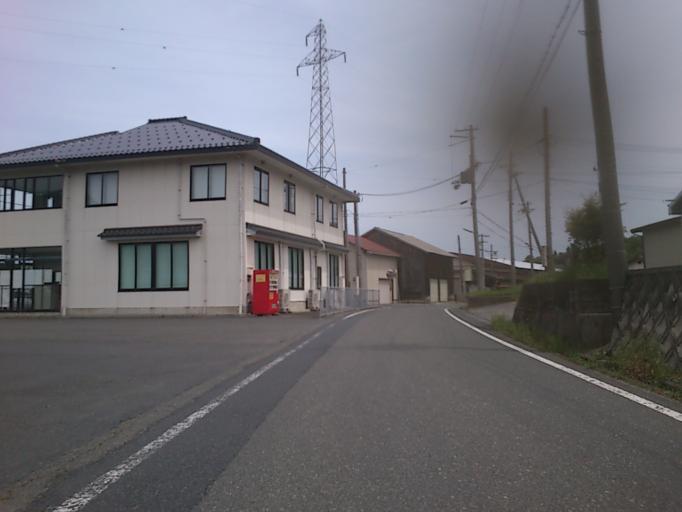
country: JP
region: Kyoto
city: Miyazu
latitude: 35.6016
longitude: 135.0486
